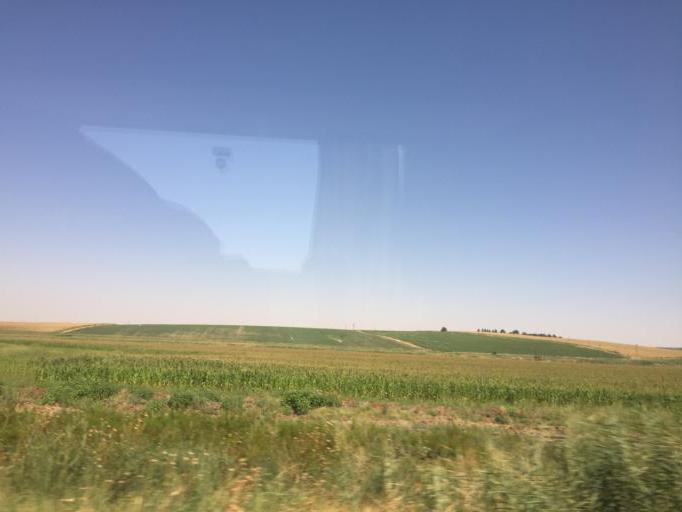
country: TR
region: Diyarbakir
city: Tepe
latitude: 37.8505
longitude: 40.7451
